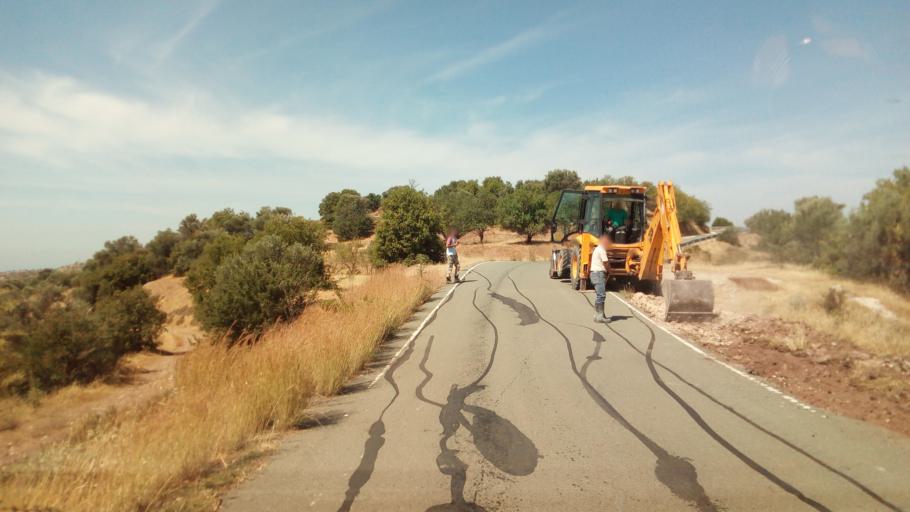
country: CY
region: Limassol
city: Pissouri
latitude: 34.8025
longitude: 32.6431
